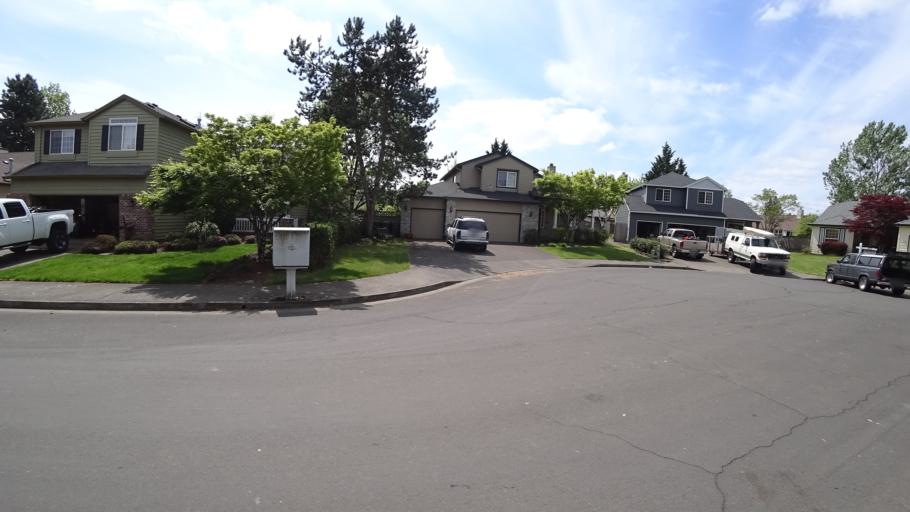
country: US
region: Oregon
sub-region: Washington County
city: Hillsboro
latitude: 45.5400
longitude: -122.9931
